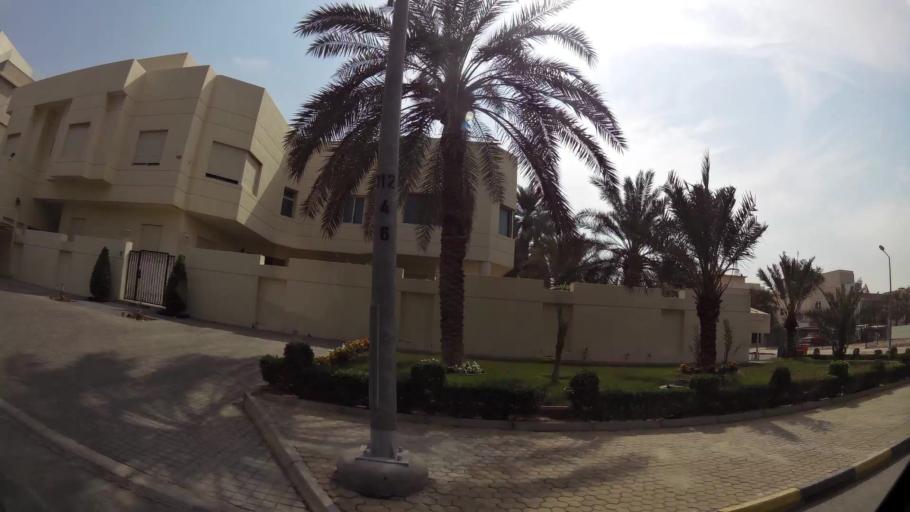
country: KW
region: Al Asimah
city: Ash Shamiyah
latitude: 29.3461
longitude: 47.9764
